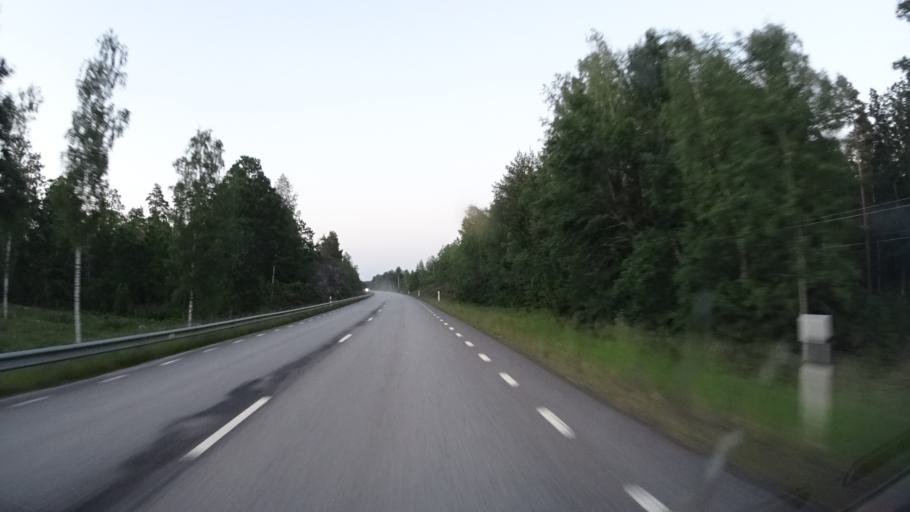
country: SE
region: Kalmar
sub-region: Hogsby Kommun
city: Hoegsby
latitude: 57.2651
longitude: 16.1637
